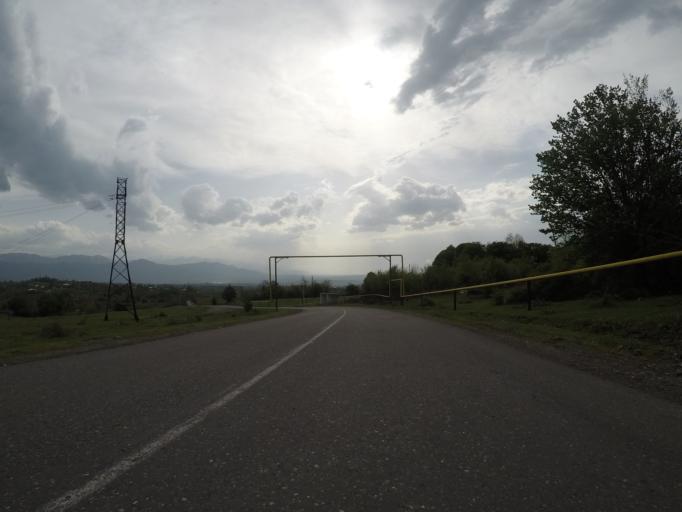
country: GE
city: Shorapani
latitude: 42.1710
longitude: 43.1263
